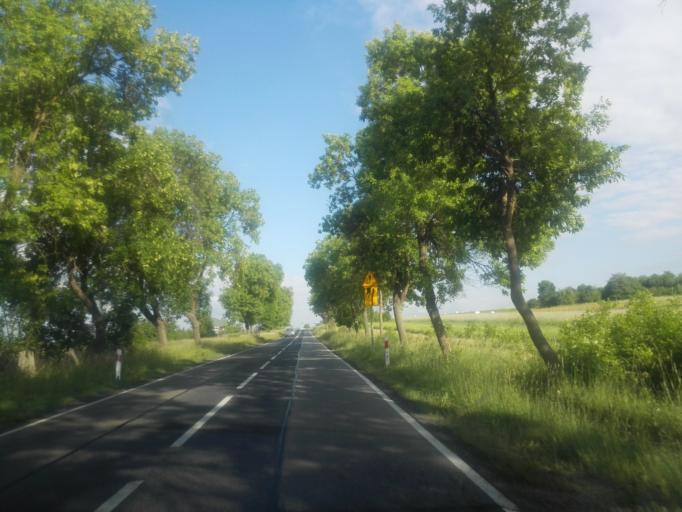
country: PL
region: Silesian Voivodeship
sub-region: Powiat czestochowski
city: Potok Zloty
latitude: 50.7322
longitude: 19.4005
